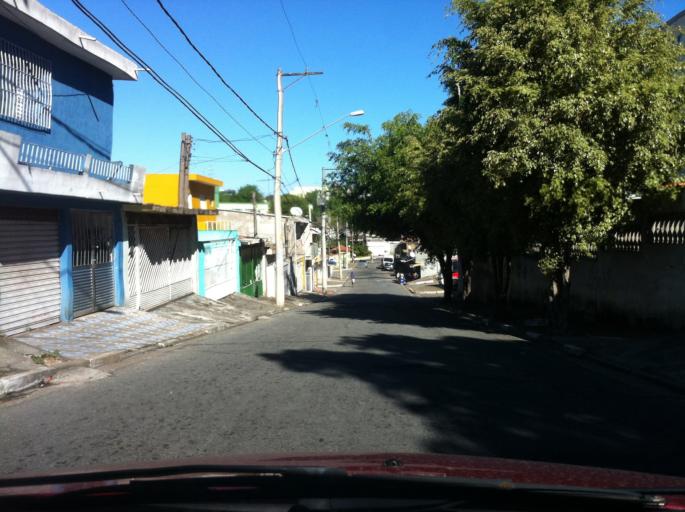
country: BR
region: Sao Paulo
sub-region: Ferraz De Vasconcelos
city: Ferraz de Vasconcelos
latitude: -23.5505
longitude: -46.4352
